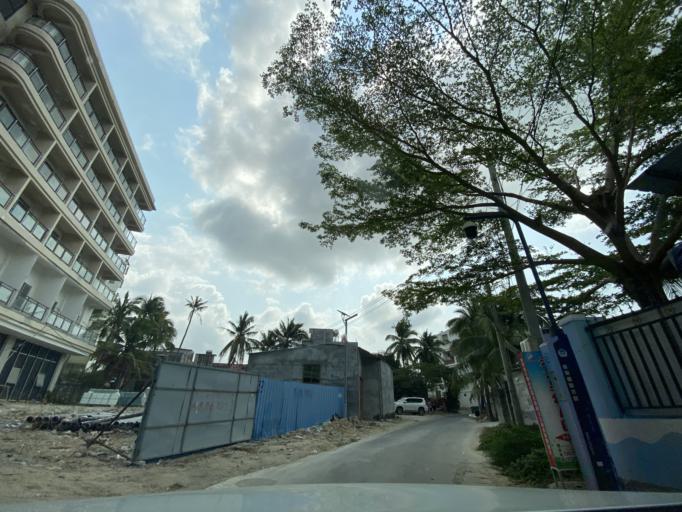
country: CN
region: Hainan
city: Yingzhou
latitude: 18.4212
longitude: 109.8537
